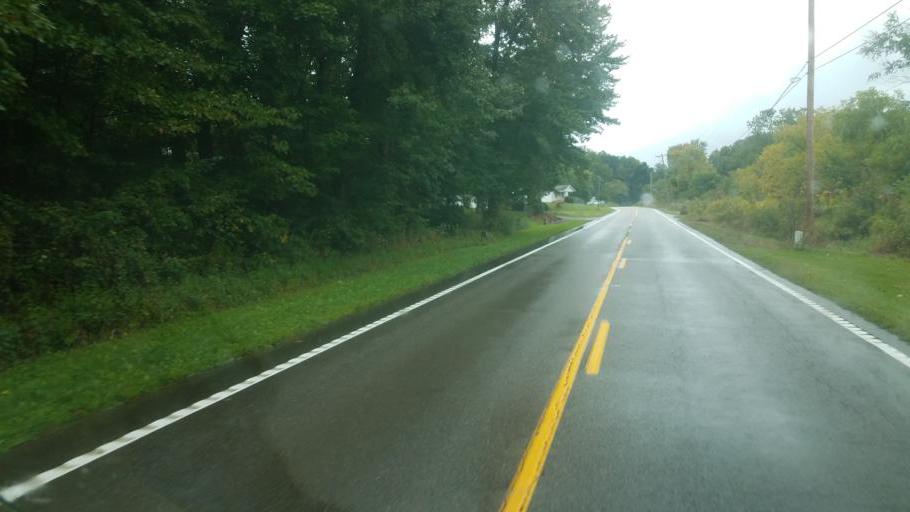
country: US
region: Ohio
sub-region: Jackson County
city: Oak Hill
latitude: 38.8599
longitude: -82.6054
